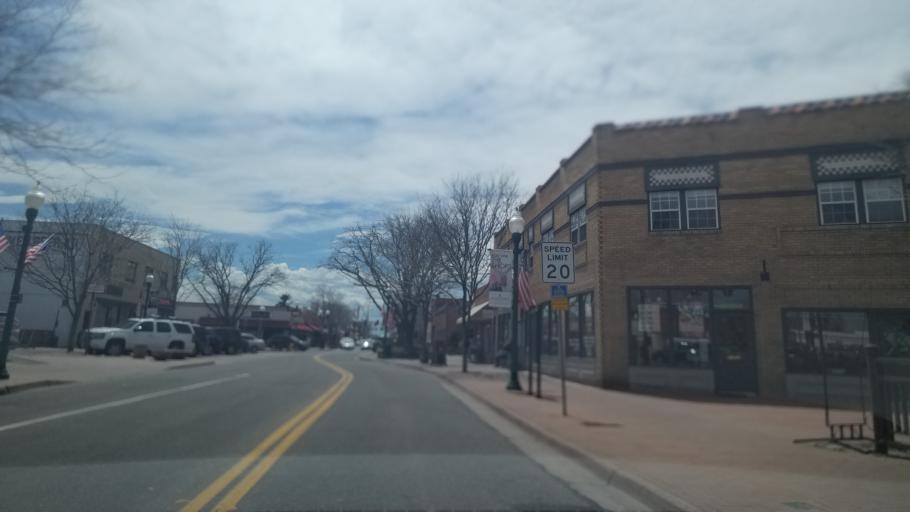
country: US
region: Colorado
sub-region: Jefferson County
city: Arvada
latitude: 39.8020
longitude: -105.0815
